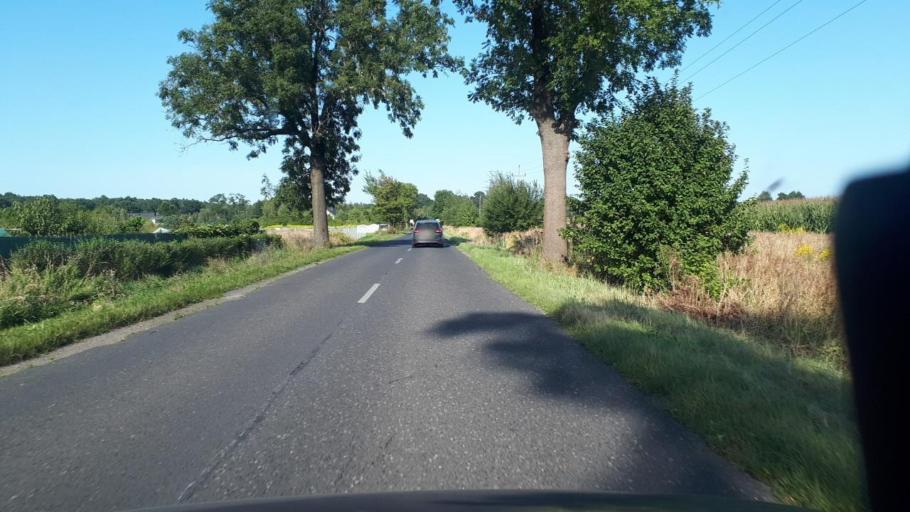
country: PL
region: Silesian Voivodeship
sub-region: Powiat tarnogorski
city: Tworog
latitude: 50.4864
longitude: 18.6986
